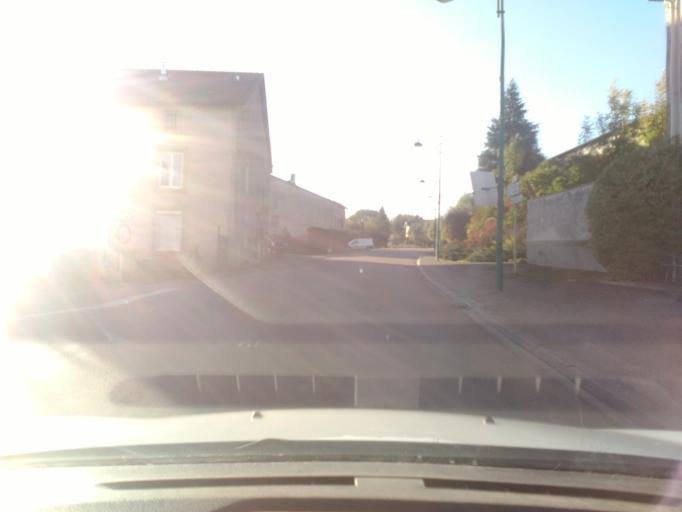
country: FR
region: Lorraine
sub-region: Departement des Vosges
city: Chatel-sur-Moselle
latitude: 48.3224
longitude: 6.4612
